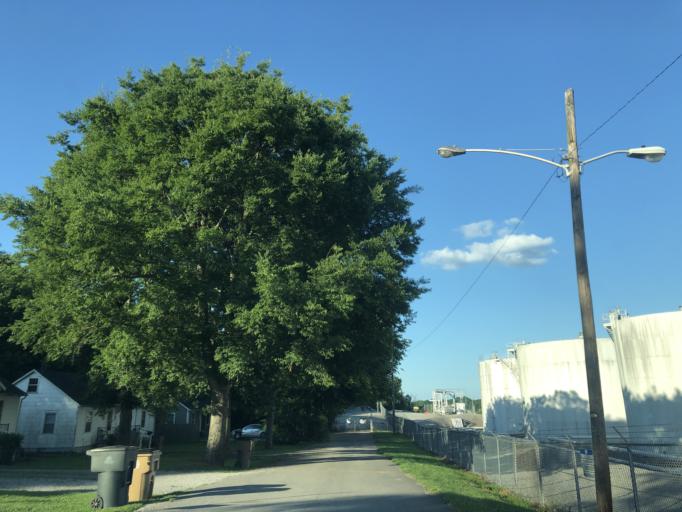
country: US
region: Tennessee
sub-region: Davidson County
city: Nashville
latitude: 36.1850
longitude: -86.8337
